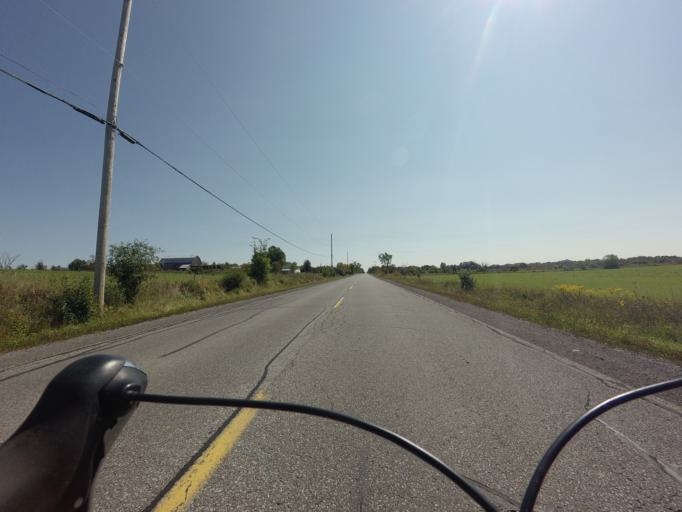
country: CA
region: Ontario
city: Bells Corners
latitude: 45.3882
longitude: -76.0020
